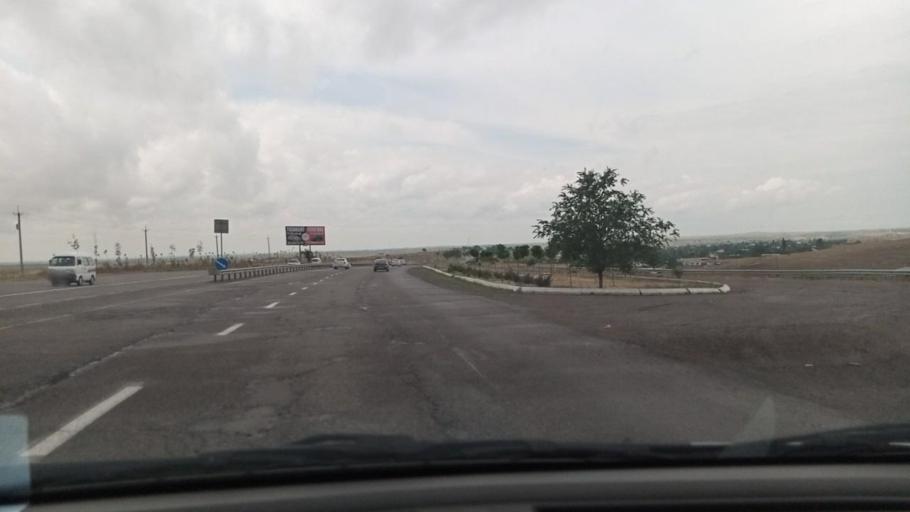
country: UZ
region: Toshkent
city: Ohangaron
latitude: 40.9681
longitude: 69.5497
